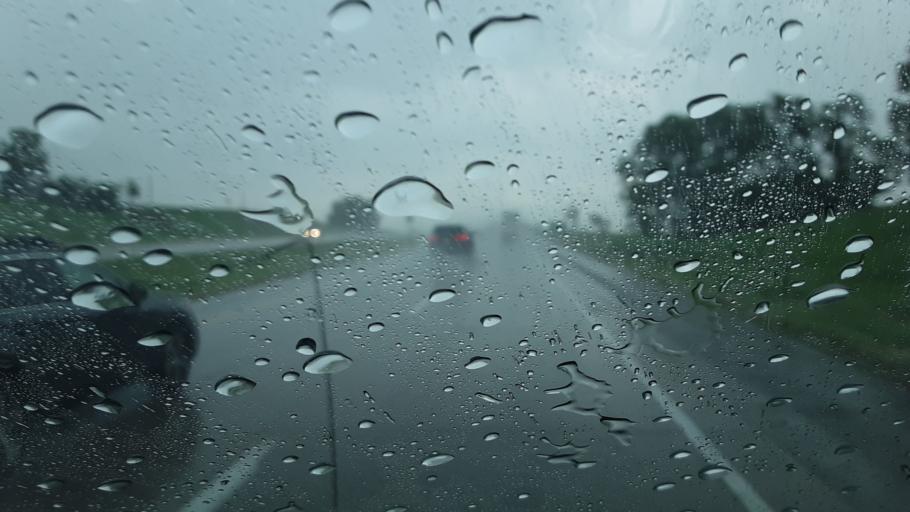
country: US
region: Iowa
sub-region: Pottawattamie County
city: Council Bluffs
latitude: 41.2692
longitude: -95.7939
